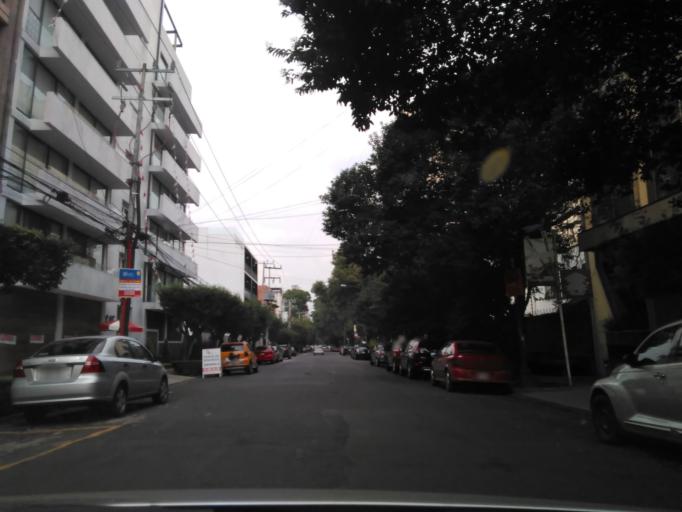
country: MX
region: Mexico City
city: Colonia del Valle
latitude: 19.3887
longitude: -99.1717
